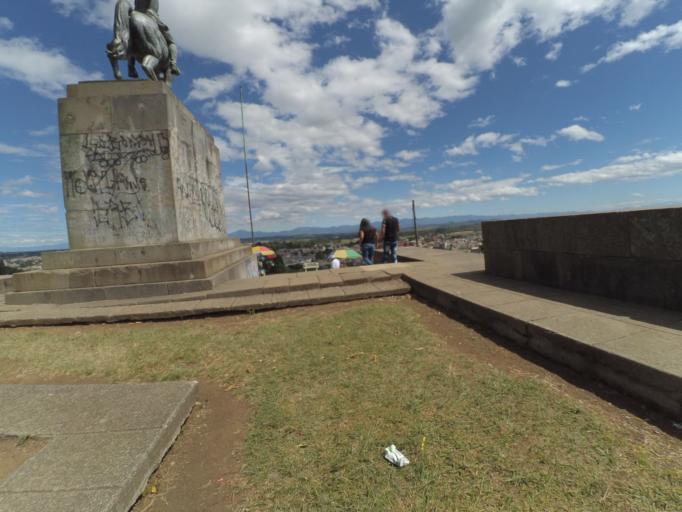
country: CO
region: Cauca
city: Popayan
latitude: 2.4447
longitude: -76.6002
